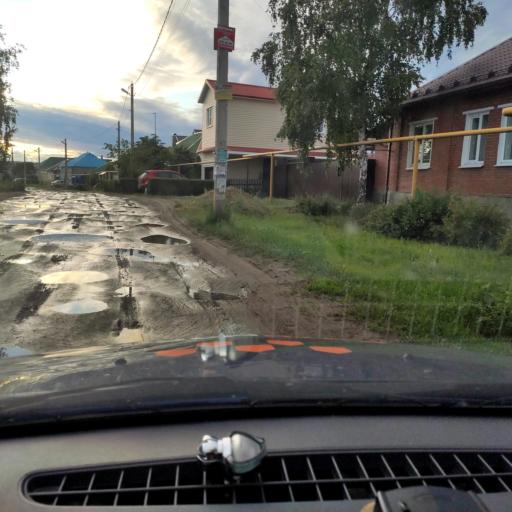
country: RU
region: Voronezj
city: Somovo
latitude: 51.7508
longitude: 39.3335
